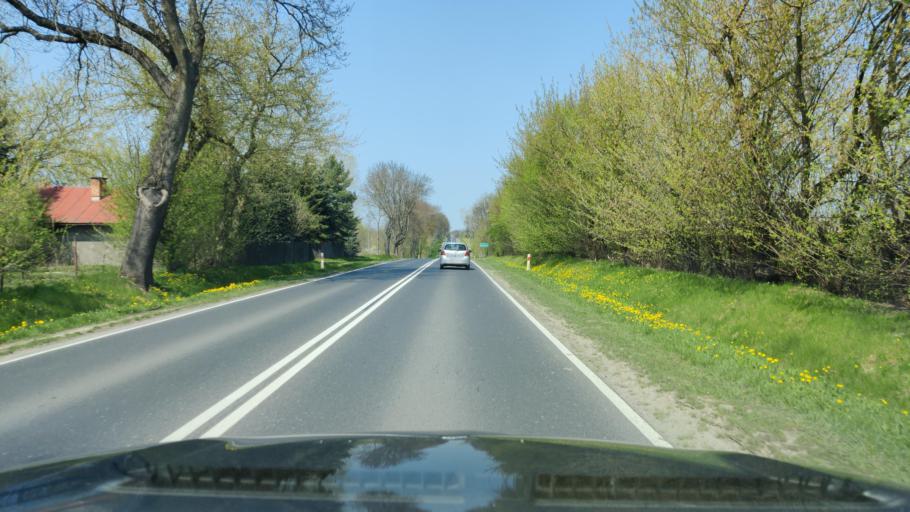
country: PL
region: Masovian Voivodeship
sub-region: Powiat pultuski
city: Pultusk
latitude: 52.6461
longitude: 21.0904
